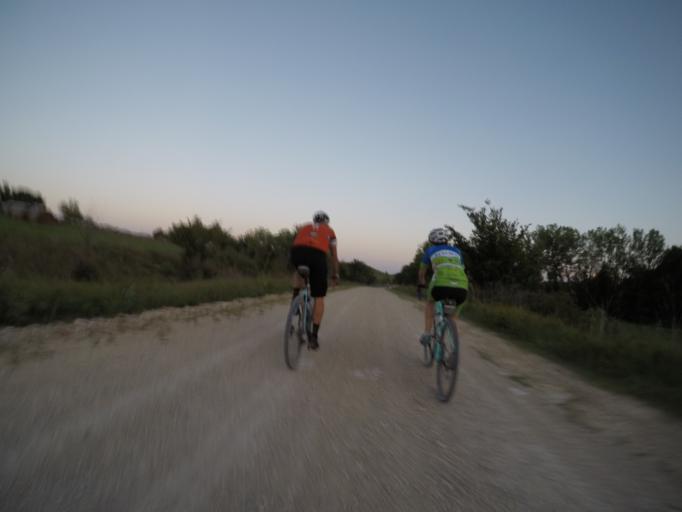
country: US
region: Kansas
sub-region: Riley County
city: Ogden
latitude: 38.9900
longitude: -96.5626
